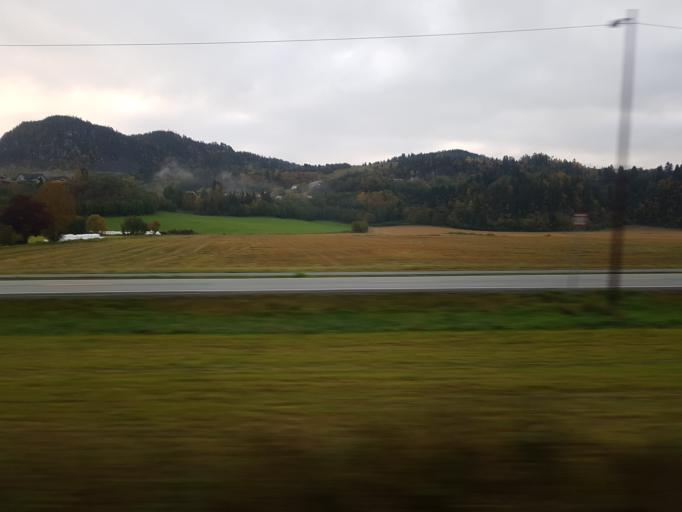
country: NO
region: Sor-Trondelag
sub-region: Melhus
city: Lundamo
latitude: 63.1286
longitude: 10.2502
